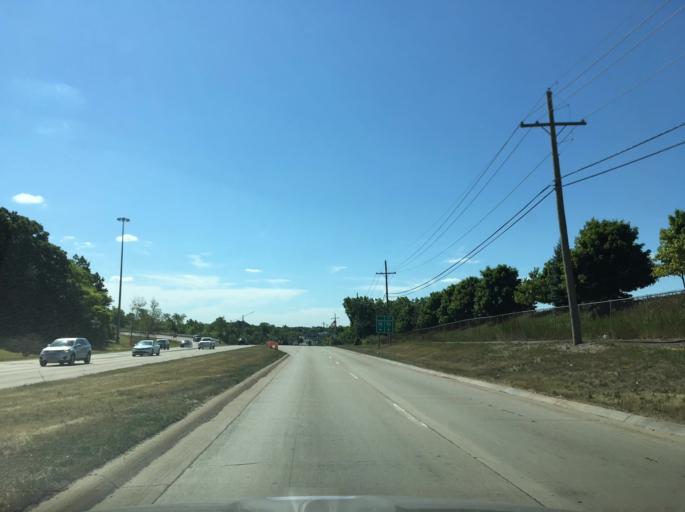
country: US
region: Michigan
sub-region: Oakland County
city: Auburn Hills
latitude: 42.6988
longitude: -83.2824
